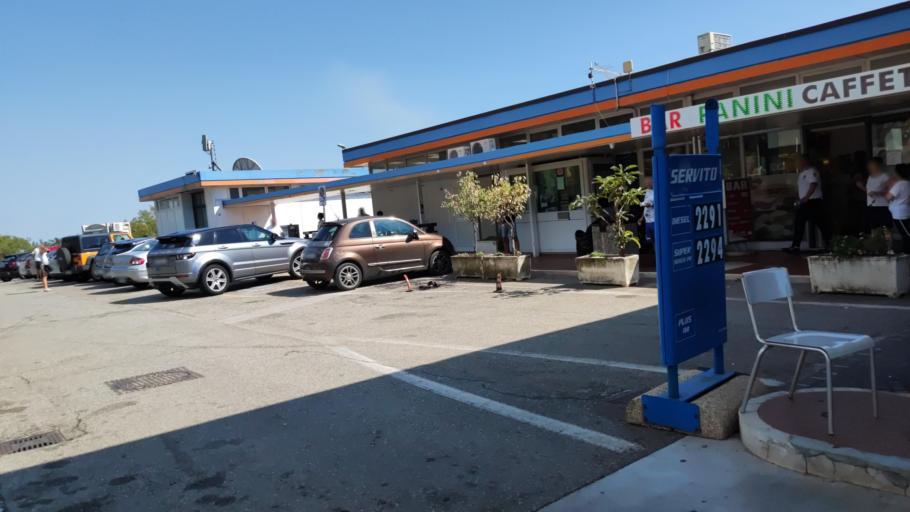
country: IT
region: Calabria
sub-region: Provincia di Cosenza
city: Frascineto
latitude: 39.8420
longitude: 16.2451
